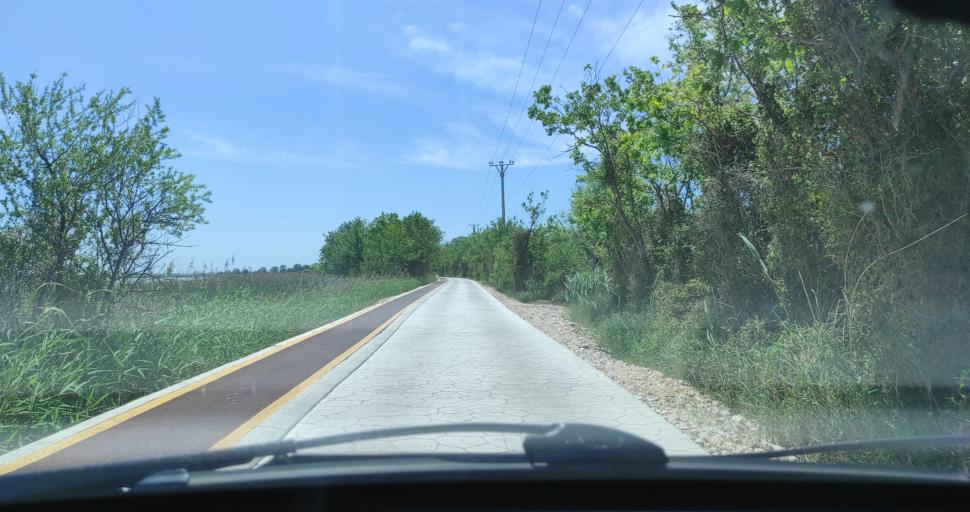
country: AL
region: Lezhe
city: Shengjin
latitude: 41.7422
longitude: 19.5821
